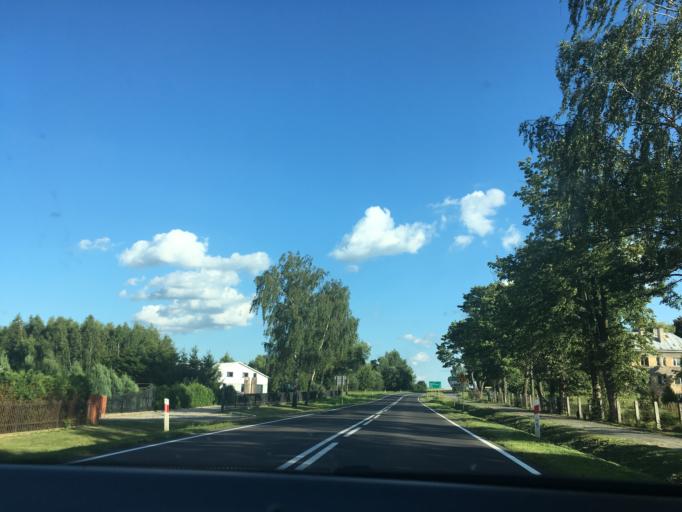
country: PL
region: Podlasie
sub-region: Powiat siemiatycki
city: Dziadkowice
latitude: 52.5619
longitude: 22.9114
